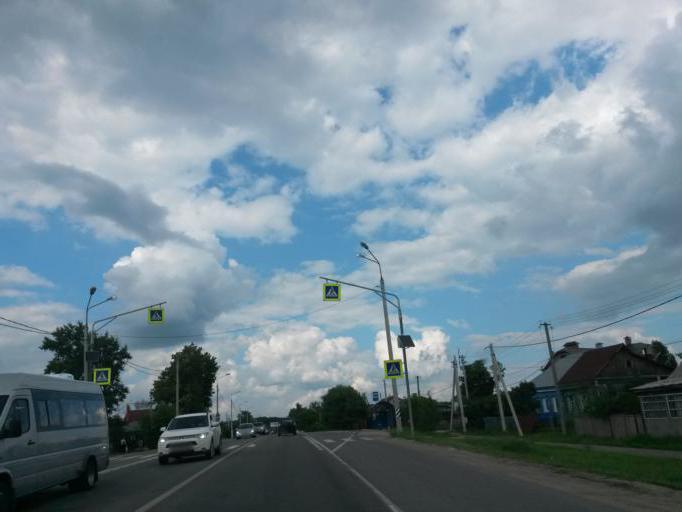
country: RU
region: Moskovskaya
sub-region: Chekhovskiy Rayon
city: Chekhov
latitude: 55.1824
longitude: 37.4921
